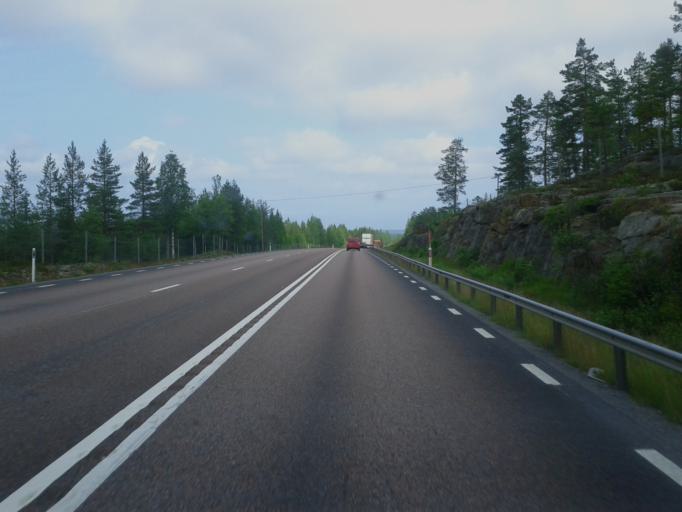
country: SE
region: Vaesterbotten
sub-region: Skelleftea Kommun
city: Burea
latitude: 64.4437
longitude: 21.2832
